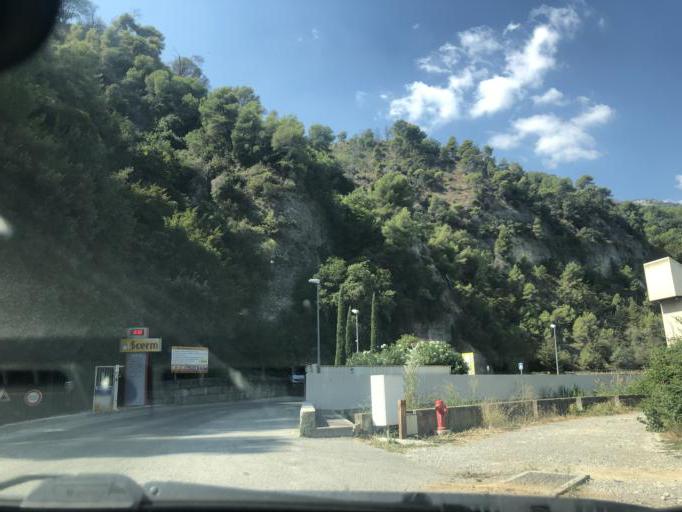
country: FR
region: Provence-Alpes-Cote d'Azur
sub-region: Departement des Alpes-Maritimes
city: Carros
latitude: 43.7935
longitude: 7.1994
